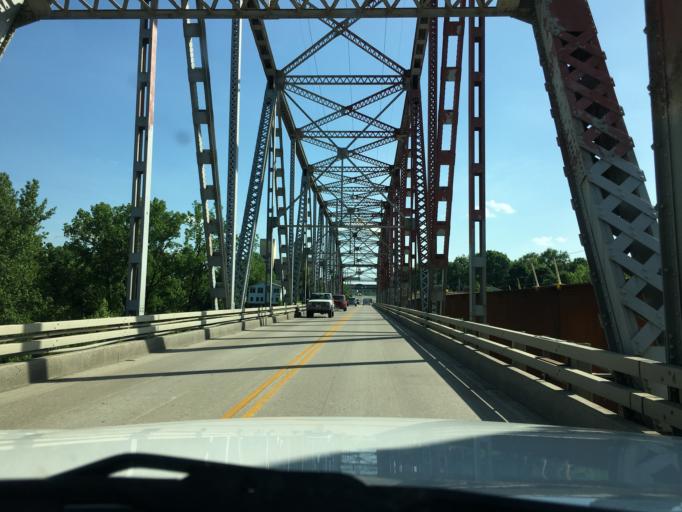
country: US
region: Missouri
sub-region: Franklin County
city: Washington
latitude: 38.5564
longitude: -90.9990
